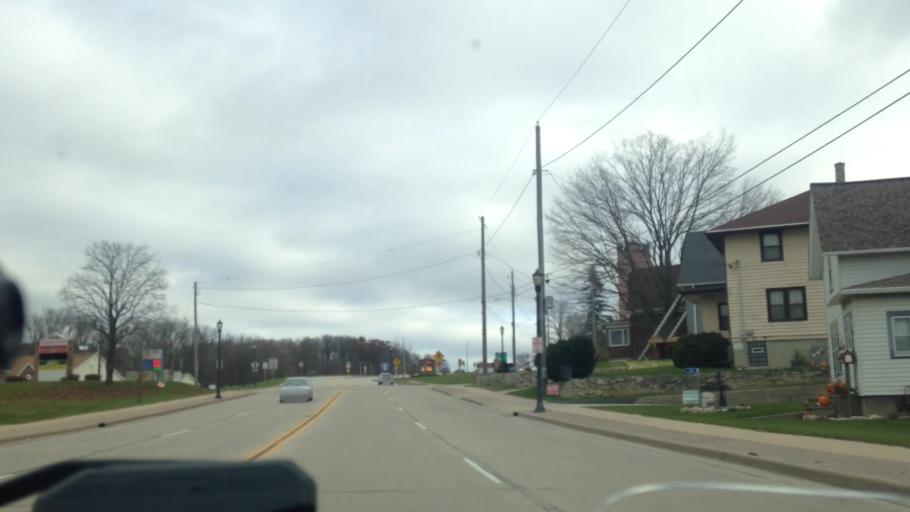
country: US
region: Wisconsin
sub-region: Washington County
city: Slinger
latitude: 43.4219
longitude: -88.3398
